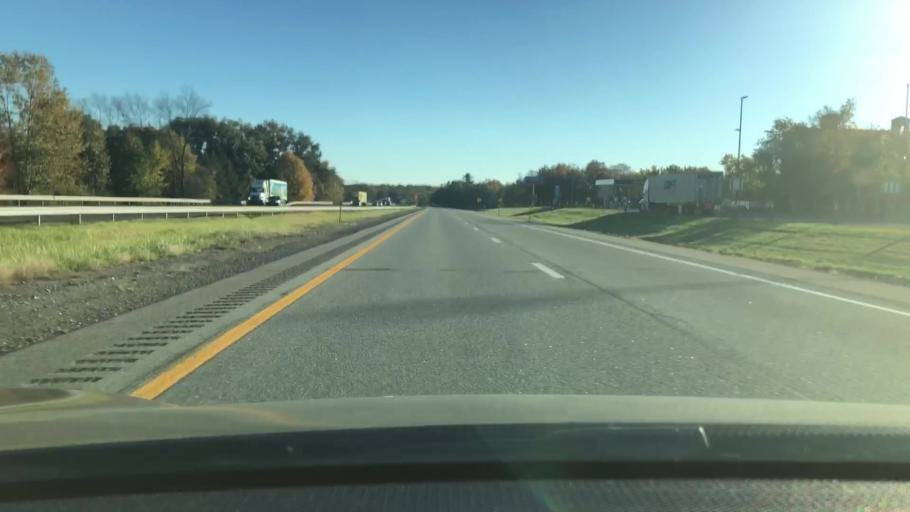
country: US
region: New York
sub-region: Ulster County
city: Plattekill
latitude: 41.5929
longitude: -74.0875
